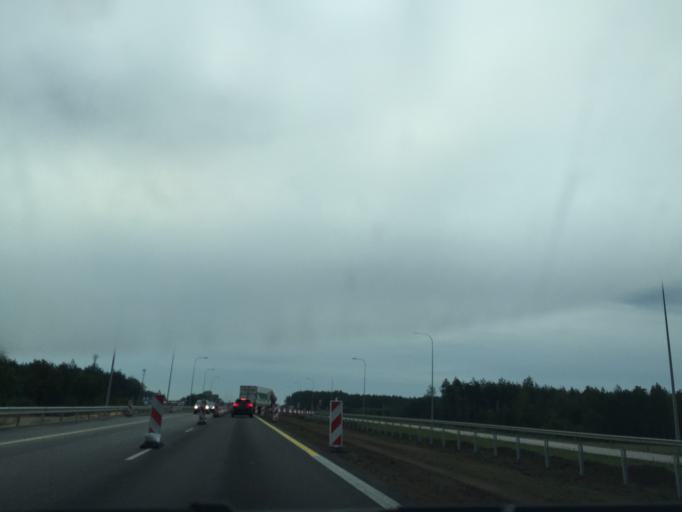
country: PL
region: Podlasie
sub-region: Powiat zambrowski
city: Szumowo
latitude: 52.9039
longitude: 22.0859
